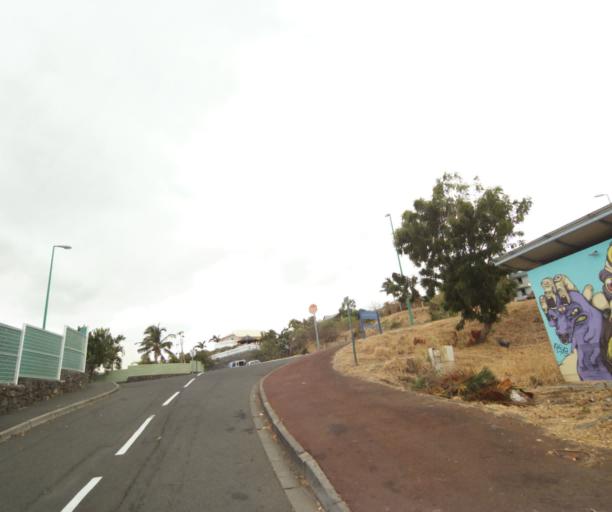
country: RE
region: Reunion
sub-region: Reunion
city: Saint-Paul
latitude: -21.0604
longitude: 55.2265
